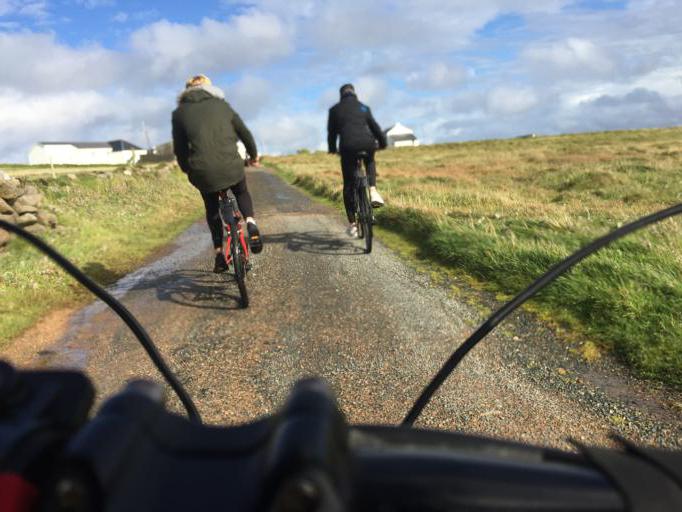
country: IE
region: Ulster
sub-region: County Donegal
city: Derrybeg
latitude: 55.2637
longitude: -8.2359
